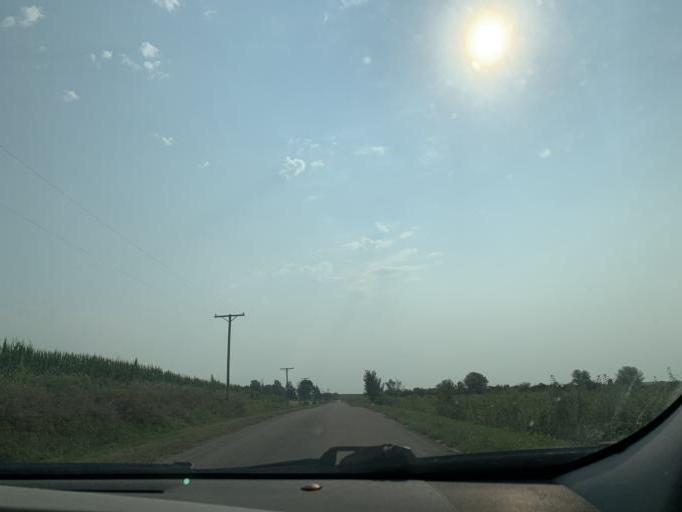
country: US
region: Illinois
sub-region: Whiteside County
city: Morrison
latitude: 41.8769
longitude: -89.9270
